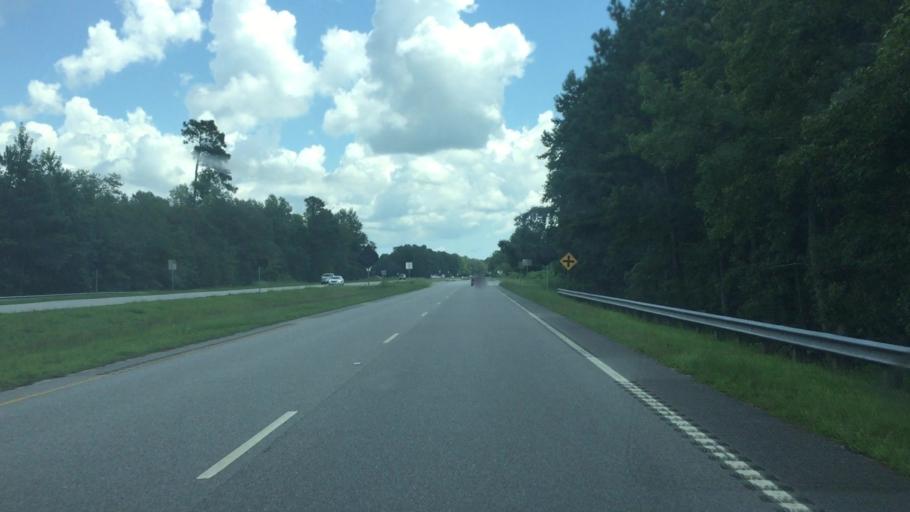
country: US
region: South Carolina
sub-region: Horry County
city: Loris
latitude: 34.0361
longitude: -78.8127
